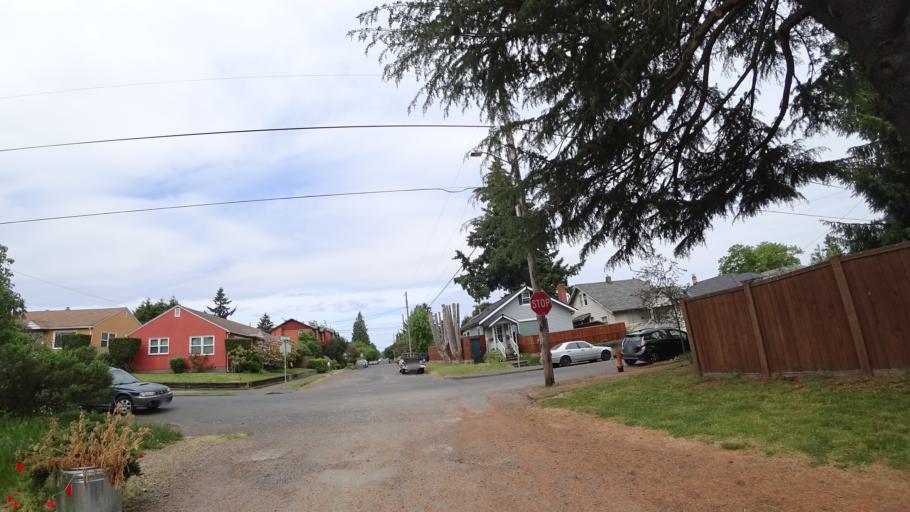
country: US
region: Oregon
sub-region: Multnomah County
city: Portland
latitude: 45.5615
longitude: -122.6387
